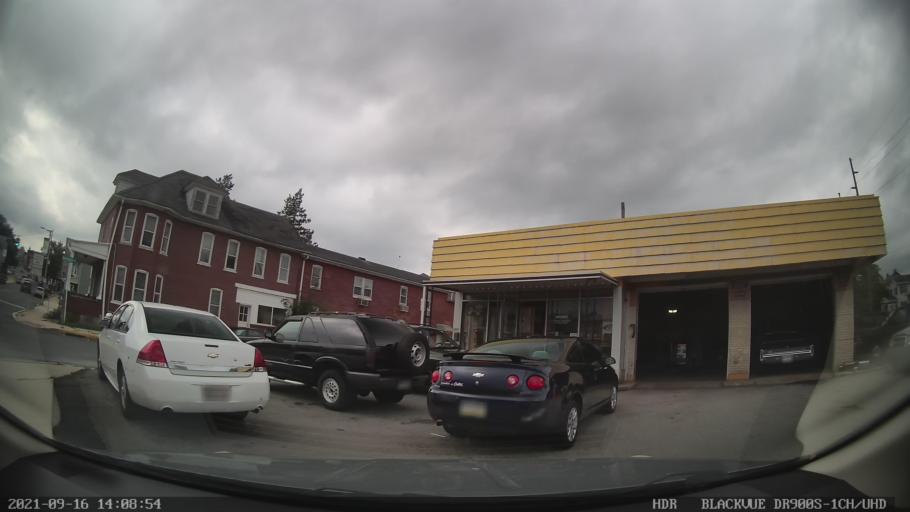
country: US
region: Pennsylvania
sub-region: Berks County
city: Kutztown
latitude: 40.5208
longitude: -75.7751
